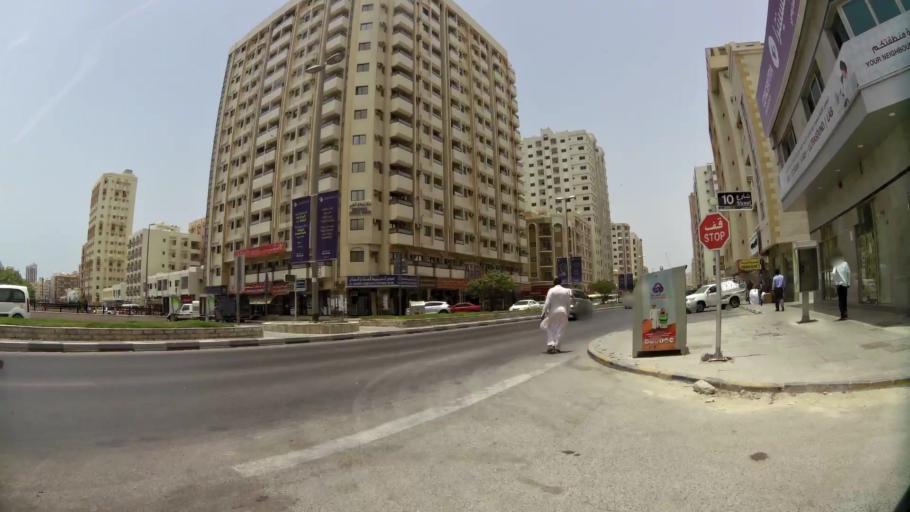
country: AE
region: Ash Shariqah
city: Sharjah
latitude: 25.3559
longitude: 55.3925
